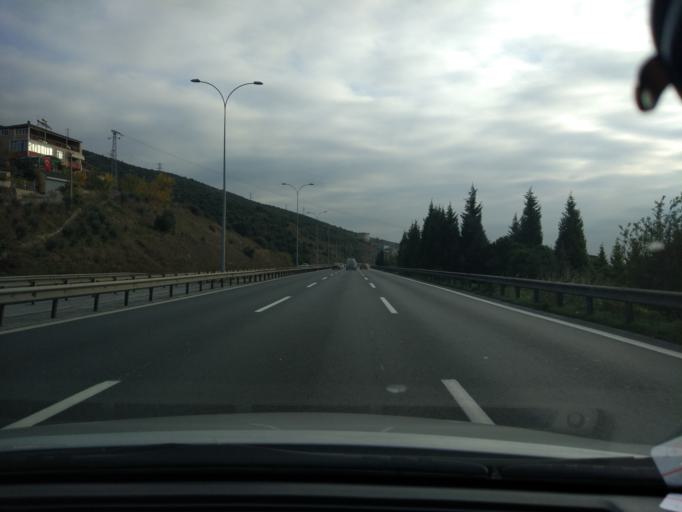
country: TR
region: Kocaeli
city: Korfez
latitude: 40.7790
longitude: 29.7100
